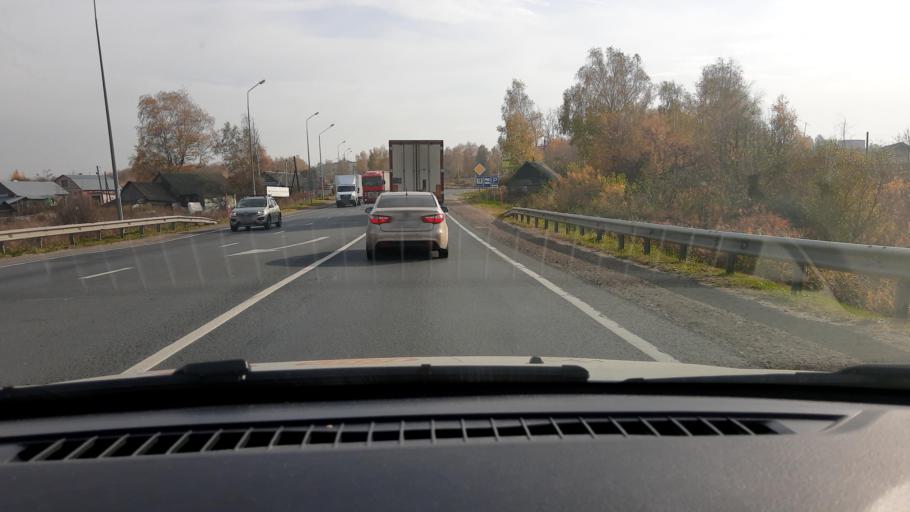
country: RU
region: Nizjnij Novgorod
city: Pamyat' Parizhskoy Kommuny
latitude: 56.0440
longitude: 44.4390
